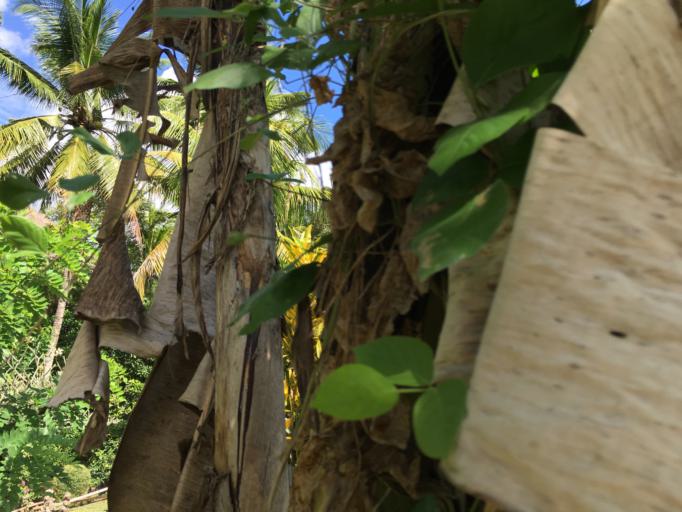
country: ID
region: Bali
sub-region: Kabupaten Gianyar
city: Ubud
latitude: -8.4958
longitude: 115.2521
